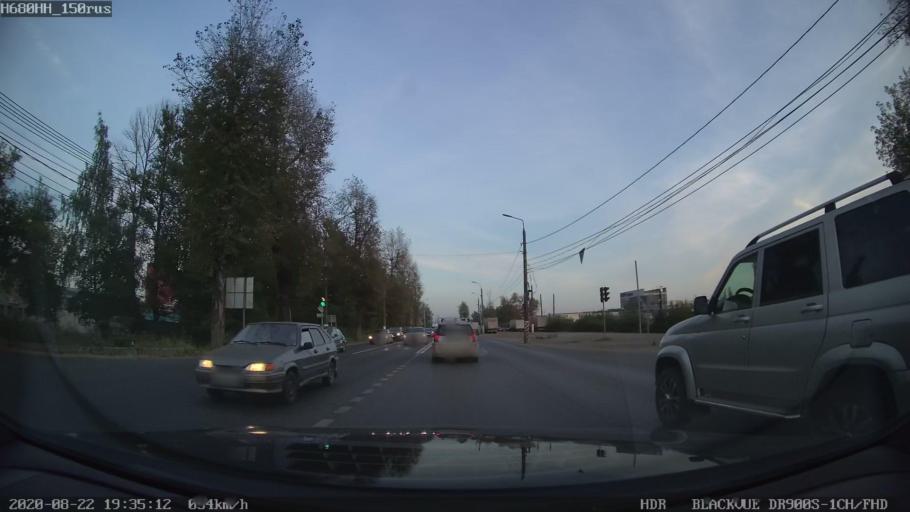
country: RU
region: Tverskaya
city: Tver
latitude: 56.8372
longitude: 35.9597
